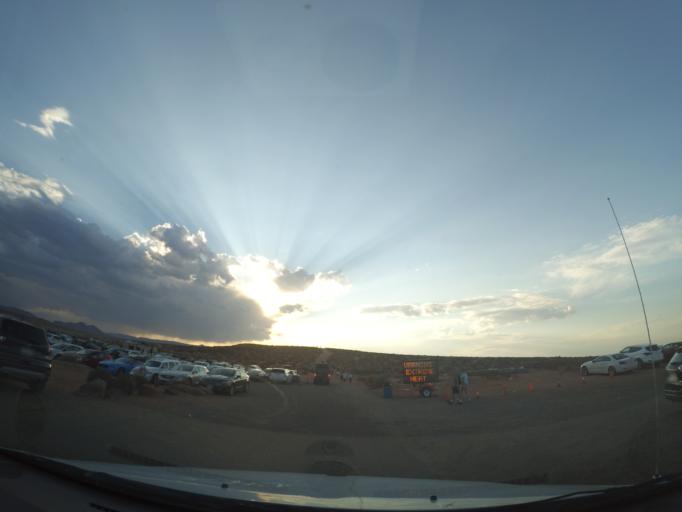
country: US
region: Arizona
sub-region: Coconino County
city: Page
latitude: 36.8766
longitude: -111.5023
